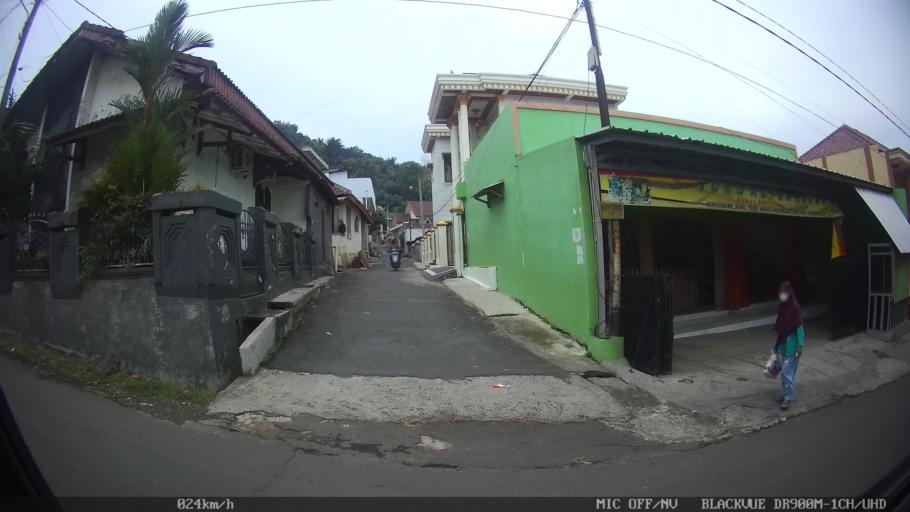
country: ID
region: Lampung
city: Bandarlampung
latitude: -5.4093
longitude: 105.2466
